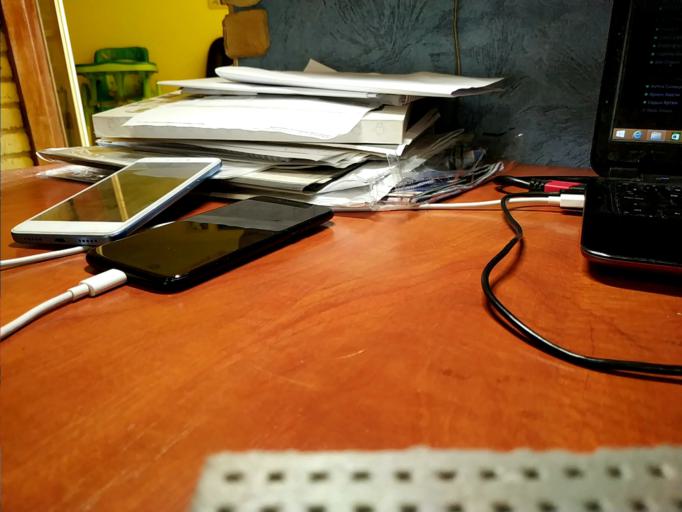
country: RU
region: Tverskaya
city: Spirovo
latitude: 57.4304
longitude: 35.0475
